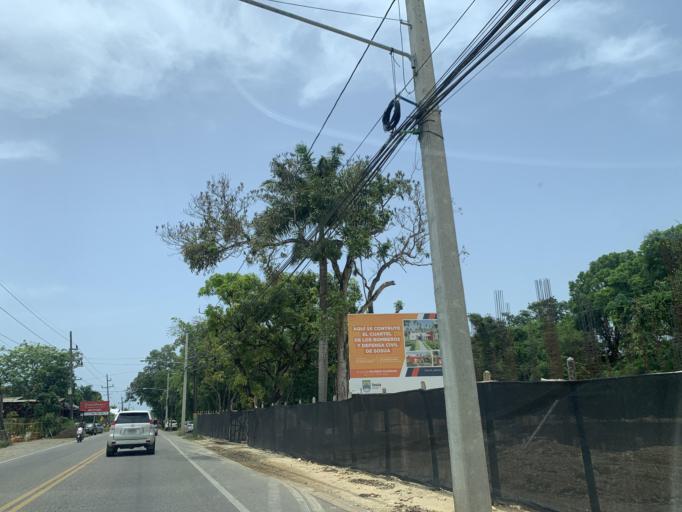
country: DO
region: Puerto Plata
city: Cabarete
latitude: 19.7712
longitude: -70.5003
